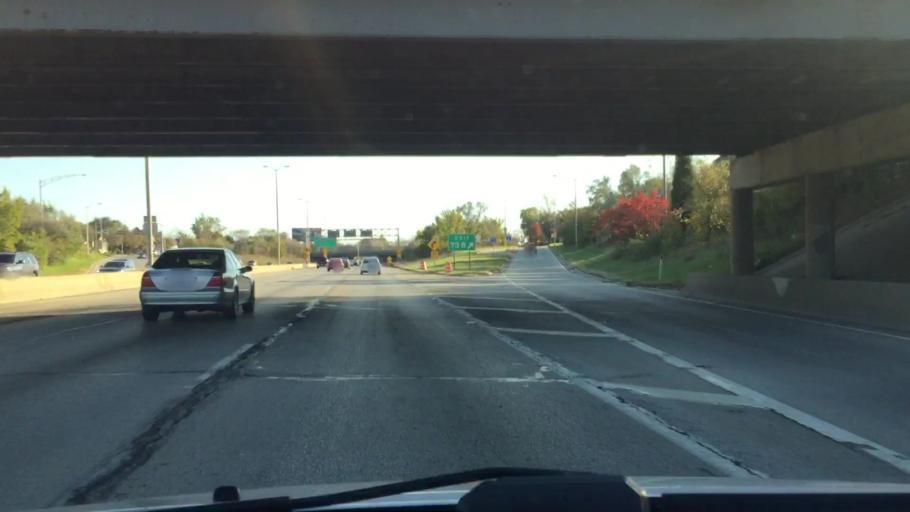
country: US
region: Wisconsin
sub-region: Milwaukee County
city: Milwaukee
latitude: 43.0641
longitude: -87.9209
